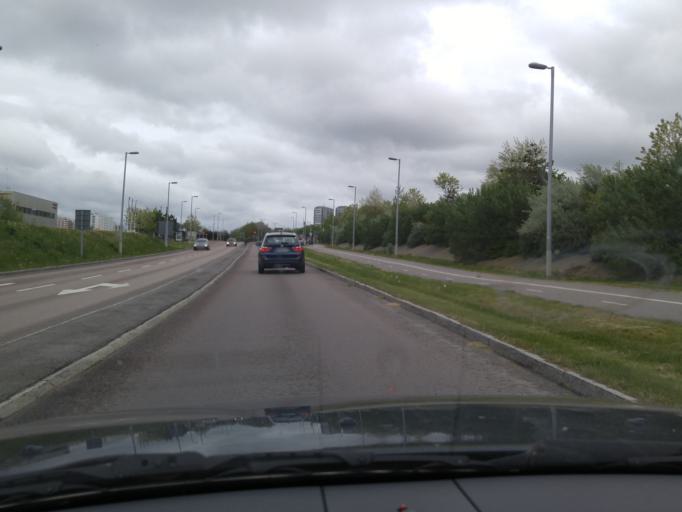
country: SE
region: Vaestra Goetaland
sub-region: Goteborg
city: Majorna
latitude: 57.6443
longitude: 11.9174
